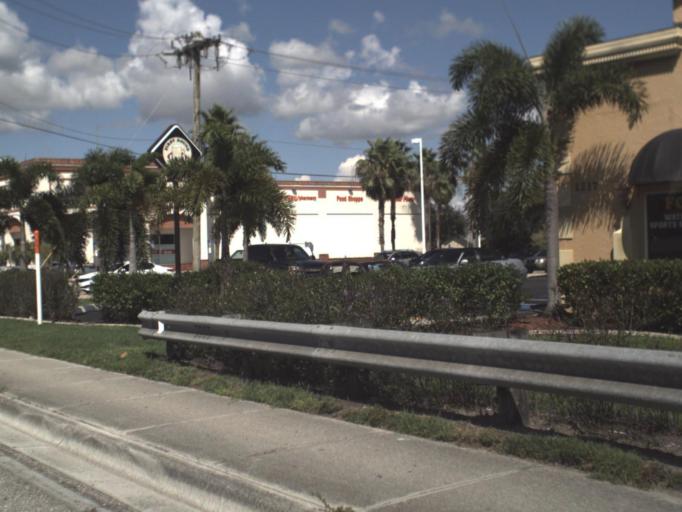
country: US
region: Florida
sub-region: Lee County
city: Lochmoor Waterway Estates
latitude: 26.6292
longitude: -81.9407
